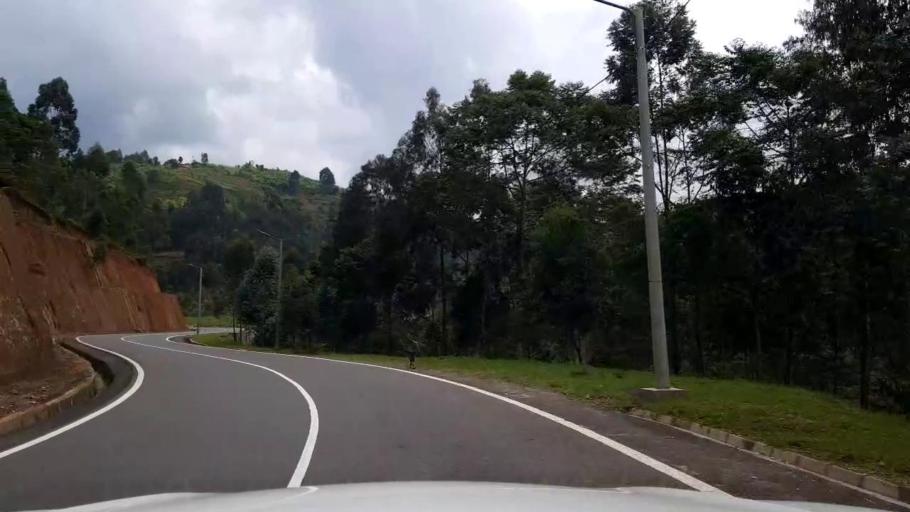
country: RW
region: Western Province
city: Kibuye
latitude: -1.9259
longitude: 29.3711
